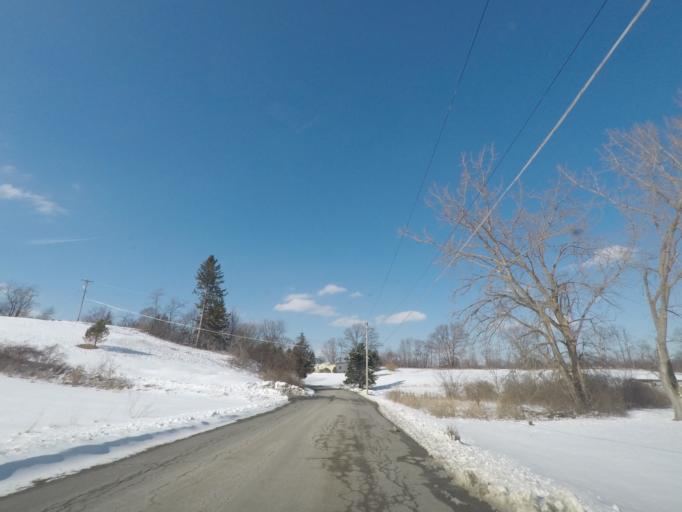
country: US
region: New York
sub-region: Saratoga County
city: Waterford
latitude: 42.8000
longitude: -73.6130
